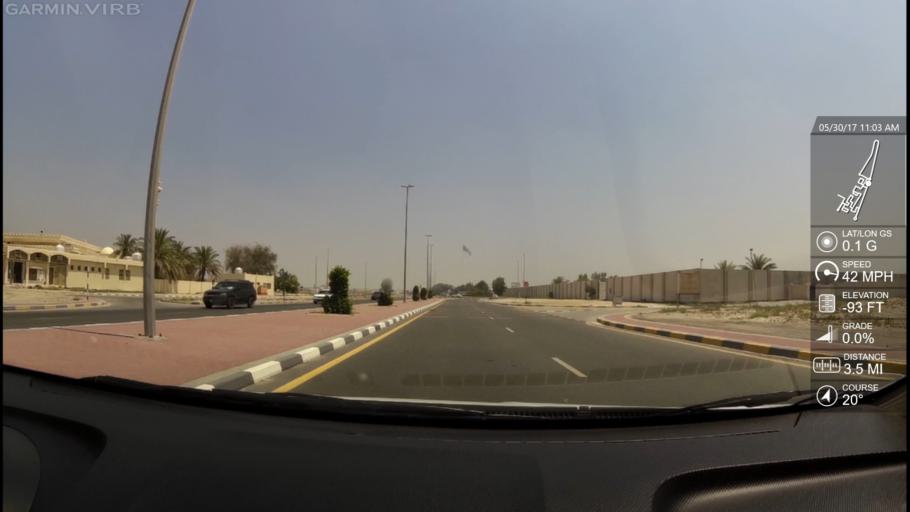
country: AE
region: Umm al Qaywayn
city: Umm al Qaywayn
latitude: 25.5596
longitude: 55.5626
